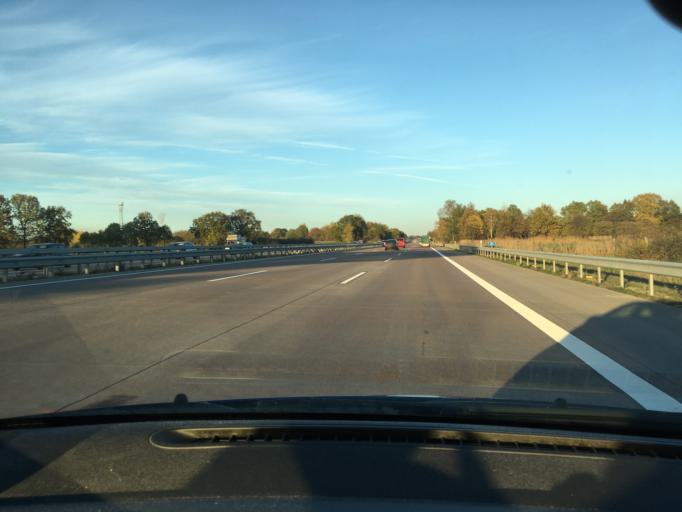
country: DE
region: Schleswig-Holstein
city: Stapelfeld
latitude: 53.5905
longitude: 10.2164
